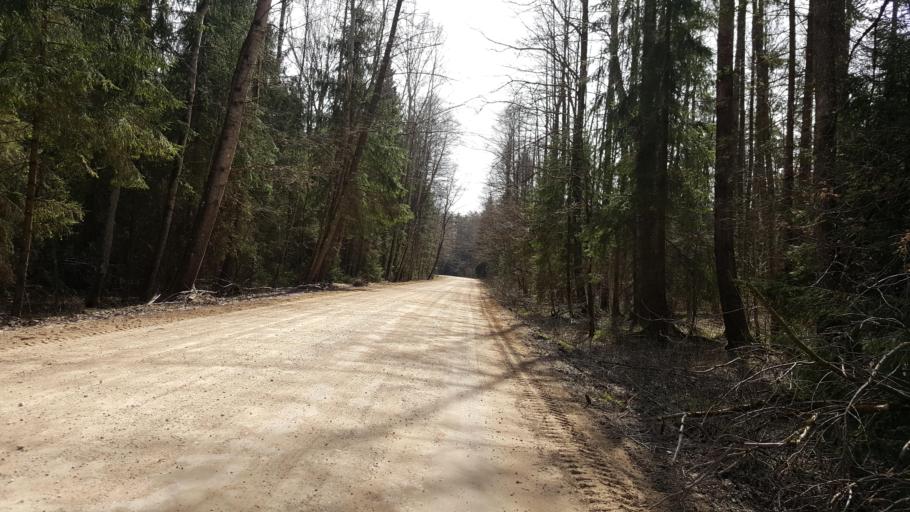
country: BY
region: Brest
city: Kamyanyuki
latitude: 52.5769
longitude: 23.7369
